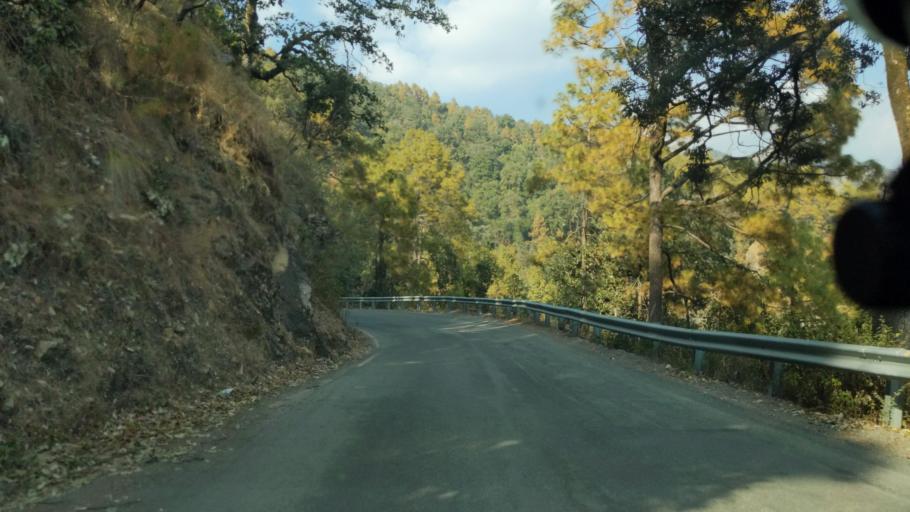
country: IN
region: Uttarakhand
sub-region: Naini Tal
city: Bhowali
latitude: 29.4000
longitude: 79.5351
